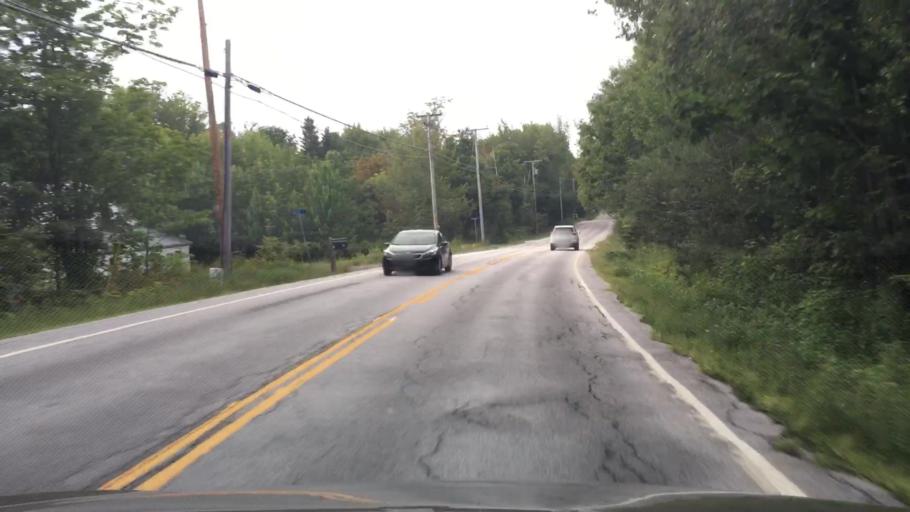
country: US
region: Maine
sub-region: Hancock County
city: Penobscot
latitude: 44.4320
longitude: -68.6057
